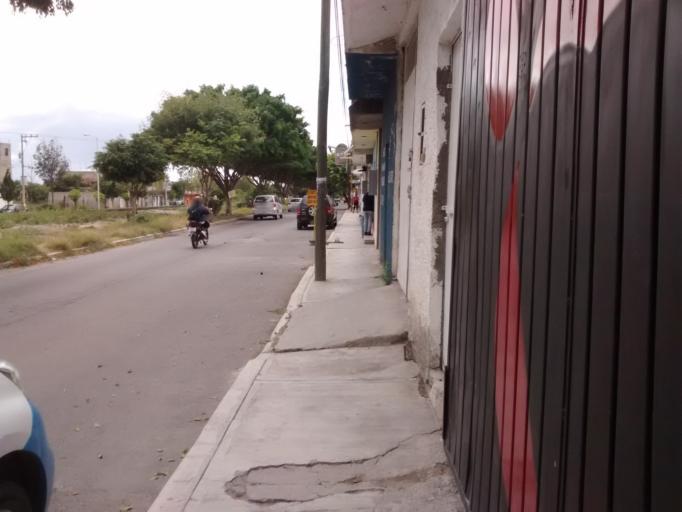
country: MX
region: Puebla
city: Tehuacan
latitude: 18.4751
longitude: -97.4084
